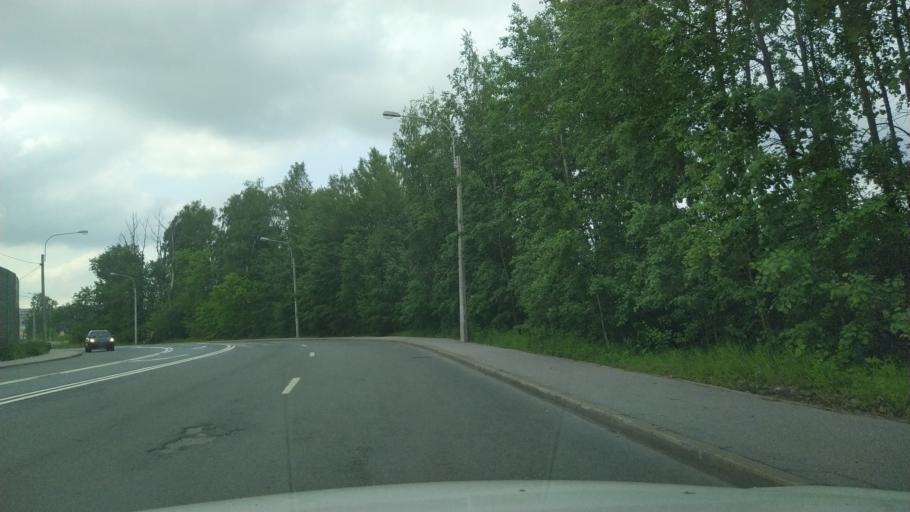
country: RU
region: St.-Petersburg
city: Krasnogvargeisky
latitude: 59.9844
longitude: 30.4404
